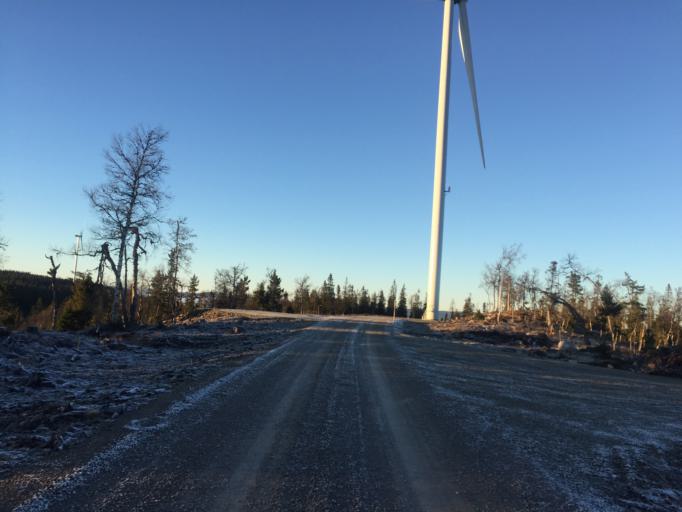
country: NO
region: Hedmark
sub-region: Elverum
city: Elverum
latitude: 61.2124
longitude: 11.7803
